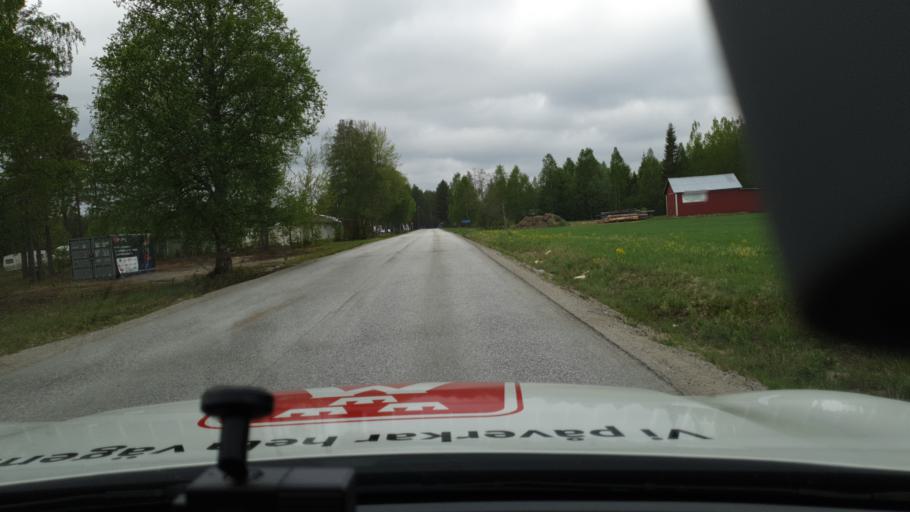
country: SE
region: Vaesterbotten
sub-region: Vindelns Kommun
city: Vindeln
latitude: 64.1803
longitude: 19.7167
